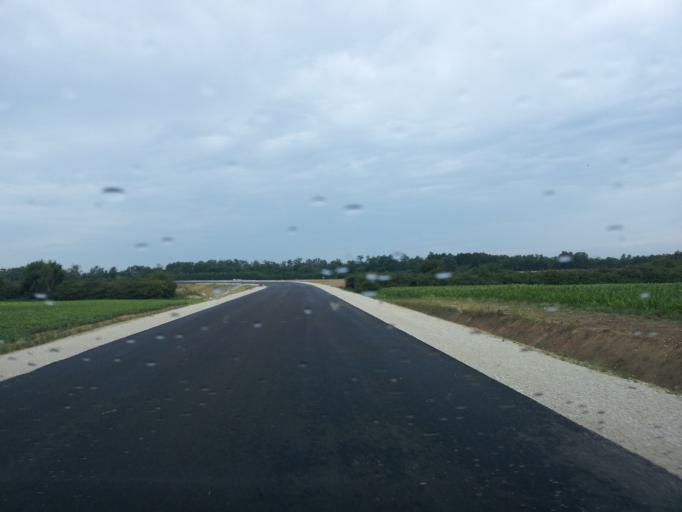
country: HU
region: Vas
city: Kormend
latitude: 46.9558
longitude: 16.6088
